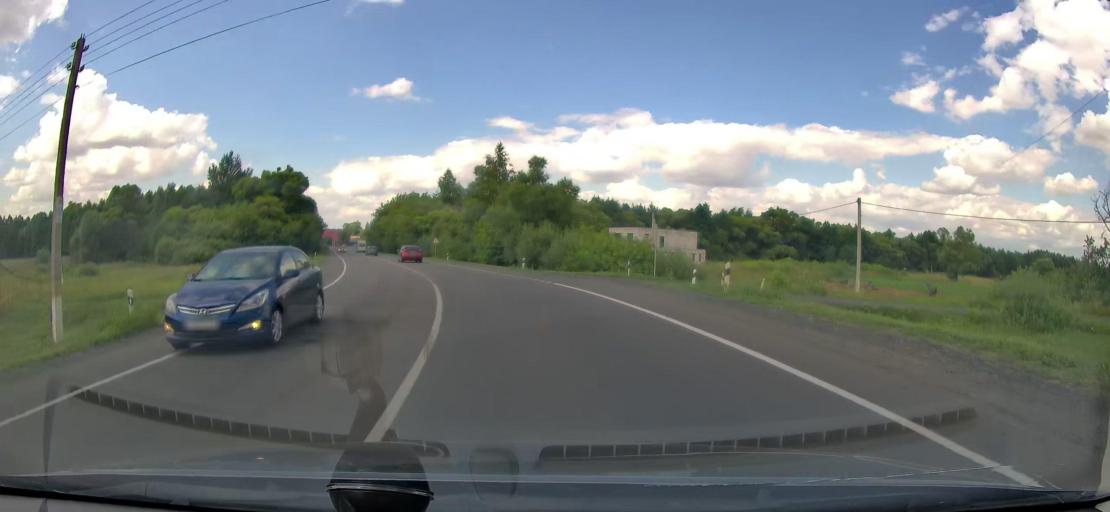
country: RU
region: Kursk
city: Zolotukhino
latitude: 51.9235
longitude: 36.3074
